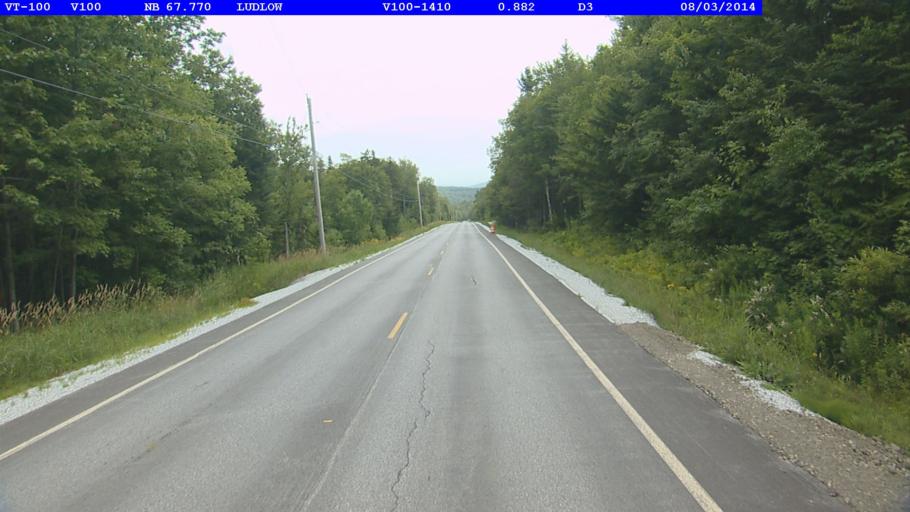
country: US
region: Vermont
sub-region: Windsor County
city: Chester
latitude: 43.3529
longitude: -72.7410
